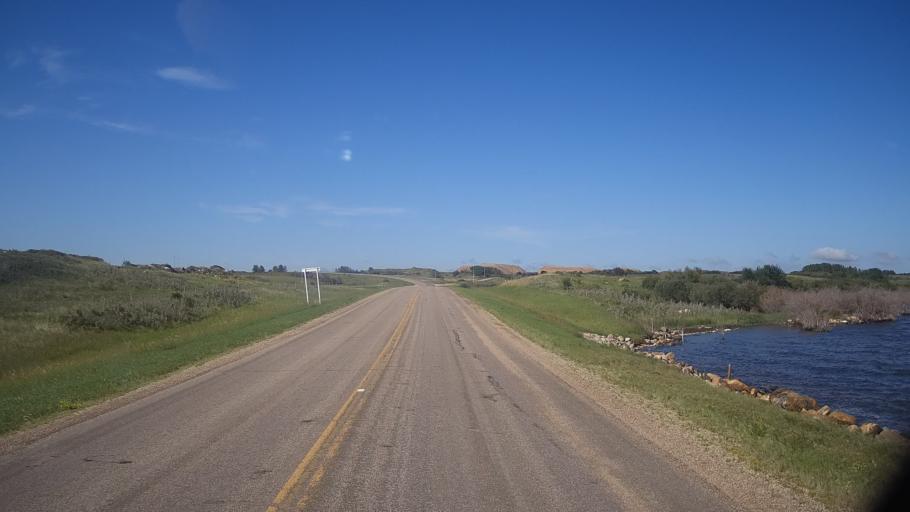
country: CA
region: Saskatchewan
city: Watrous
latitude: 51.7105
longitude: -105.3742
